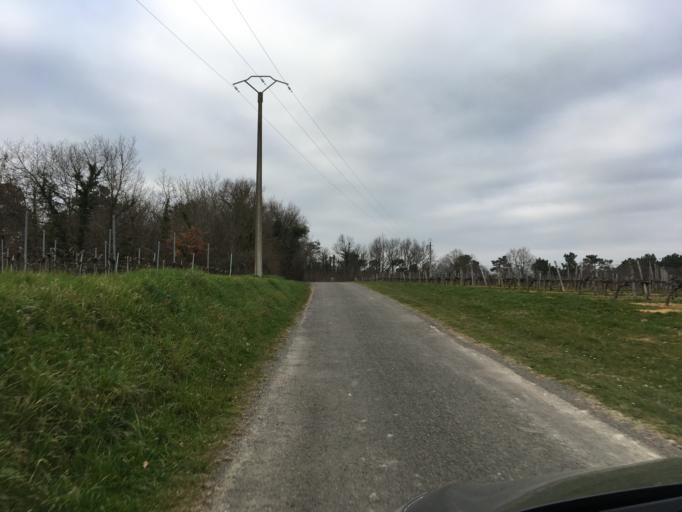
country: FR
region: Aquitaine
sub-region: Departement de la Gironde
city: Saint-Ciers-sur-Gironde
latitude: 45.3109
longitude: -0.6048
